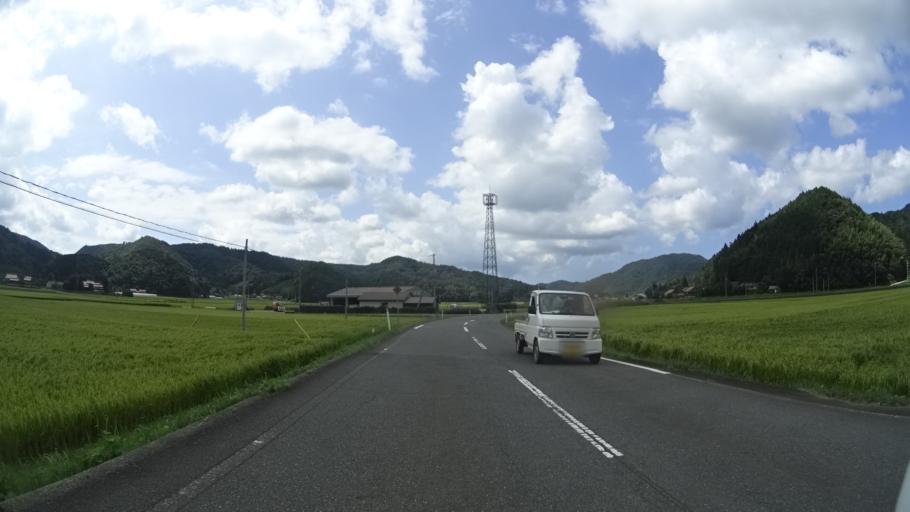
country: JP
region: Yamaguchi
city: Hagi
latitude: 34.5161
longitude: 131.6097
